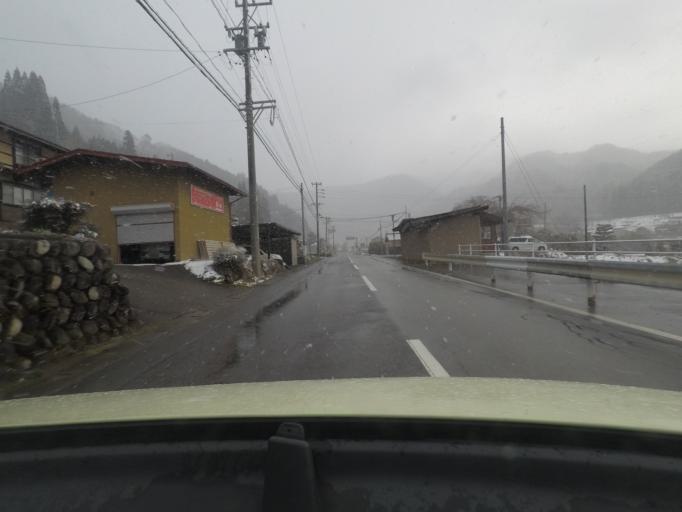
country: JP
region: Gifu
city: Takayama
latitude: 36.1367
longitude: 137.3150
